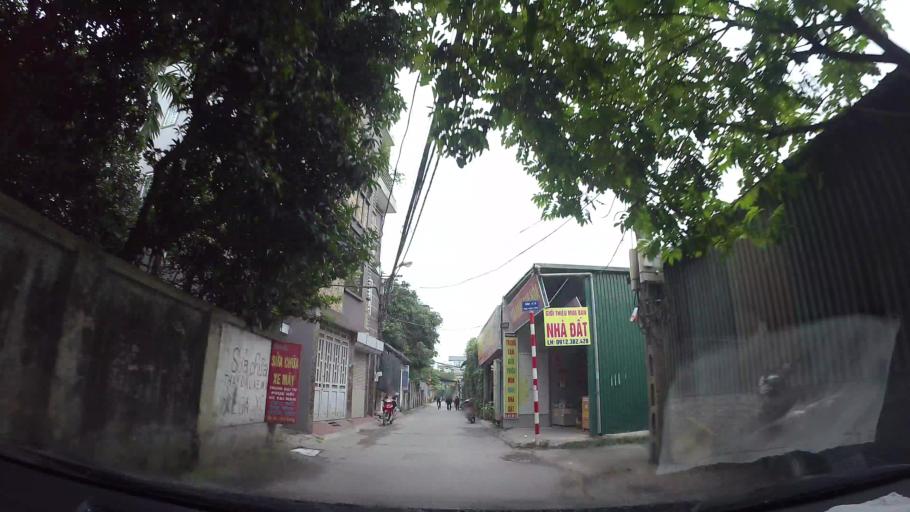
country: VN
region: Hung Yen
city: Van Giang
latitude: 20.9804
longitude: 105.8956
